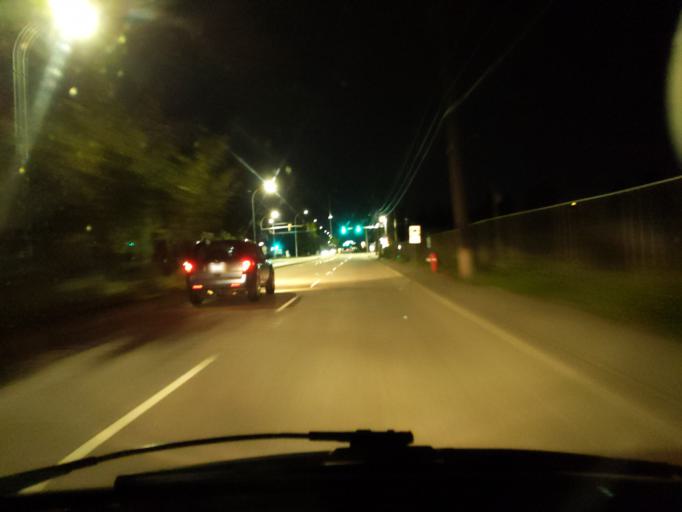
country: CA
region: British Columbia
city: Surrey
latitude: 49.1916
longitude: -122.7880
